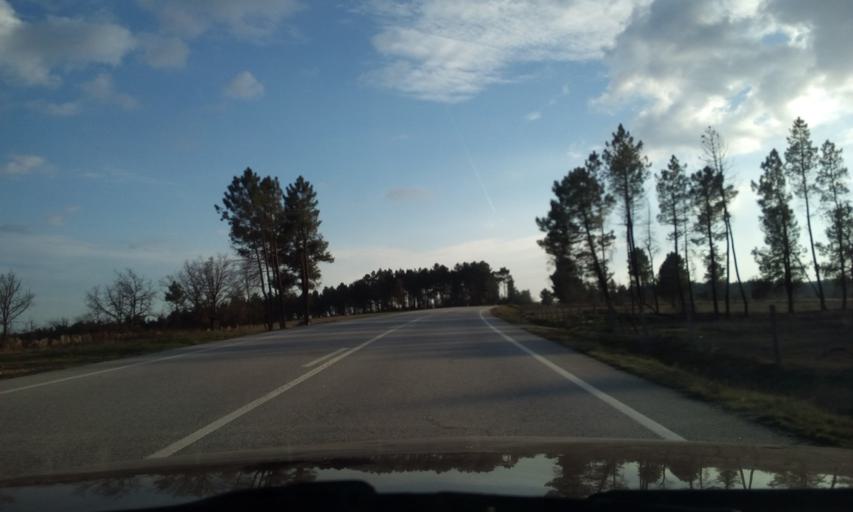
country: PT
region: Guarda
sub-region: Pinhel
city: Pinhel
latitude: 40.6443
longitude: -6.9685
